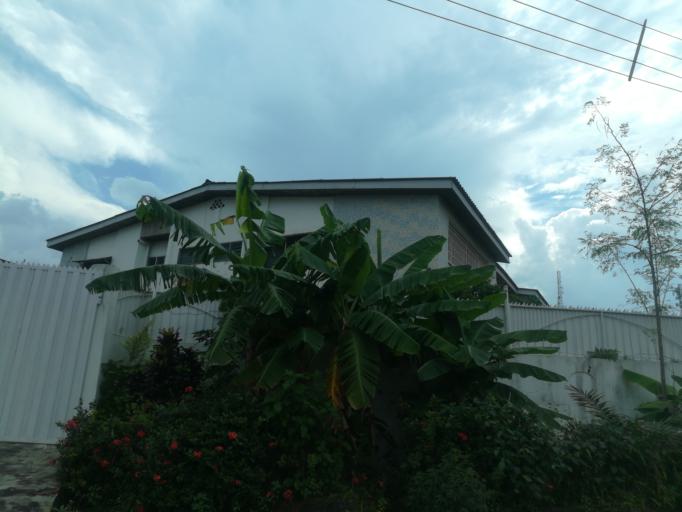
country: NG
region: Oyo
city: Ibadan
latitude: 7.4150
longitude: 3.8996
